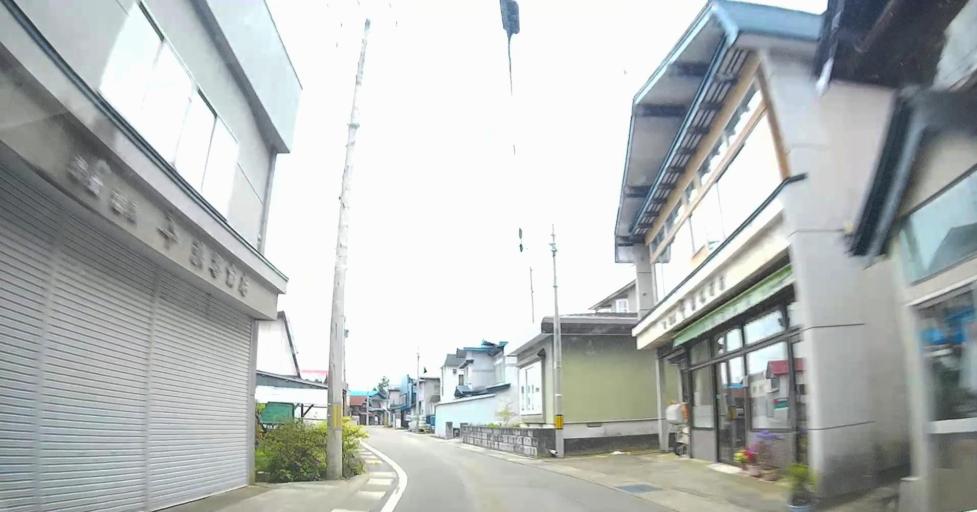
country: JP
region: Aomori
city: Shimokizukuri
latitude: 41.2013
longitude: 140.4292
